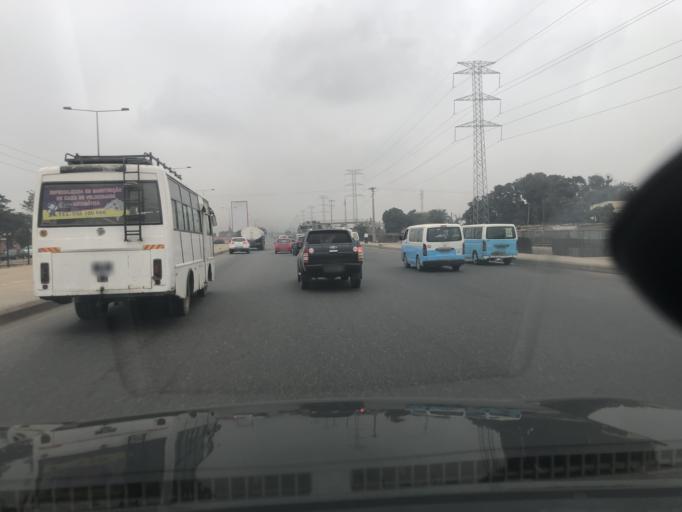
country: AO
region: Luanda
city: Luanda
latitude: -8.8632
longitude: 13.3082
